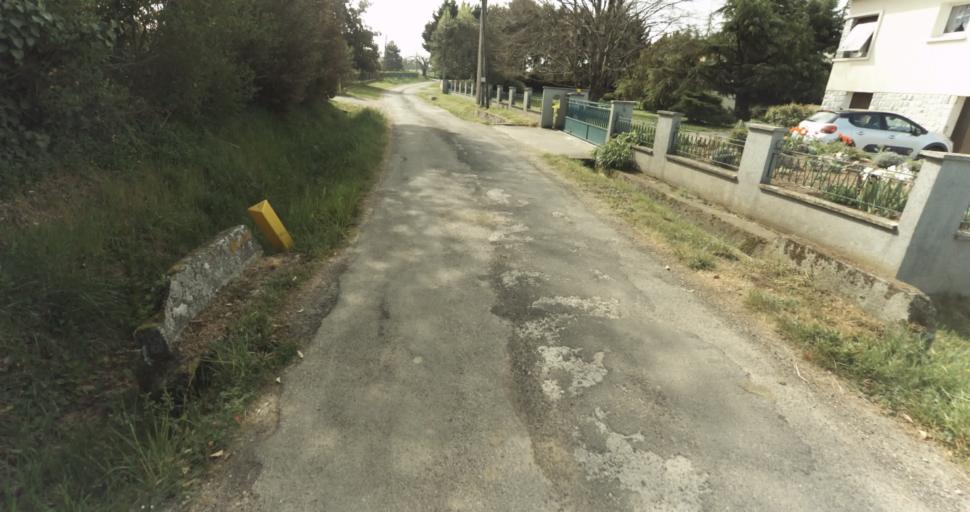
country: FR
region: Midi-Pyrenees
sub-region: Departement du Tarn-et-Garonne
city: Moissac
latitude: 44.0839
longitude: 1.0928
